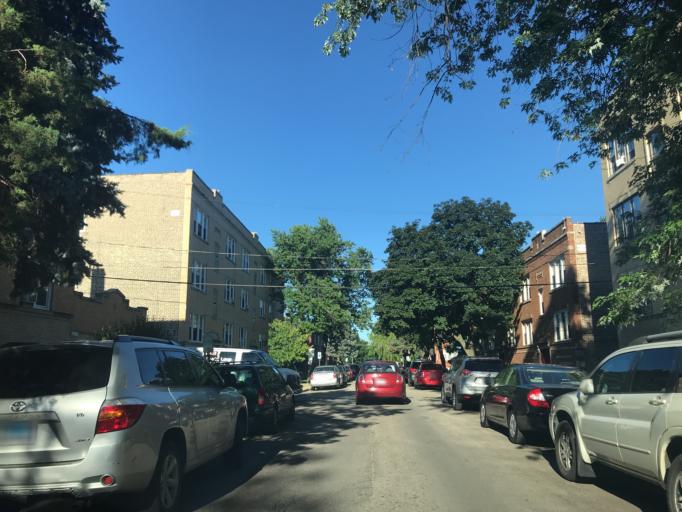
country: US
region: Illinois
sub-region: Cook County
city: Cicero
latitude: 41.8530
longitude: -87.7527
